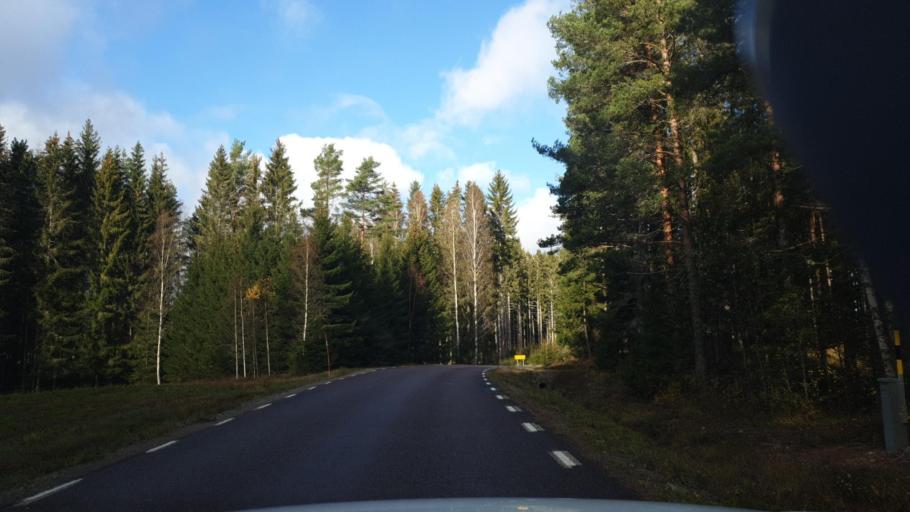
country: SE
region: Vaermland
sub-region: Grums Kommun
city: Slottsbron
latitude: 59.4939
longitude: 12.8789
